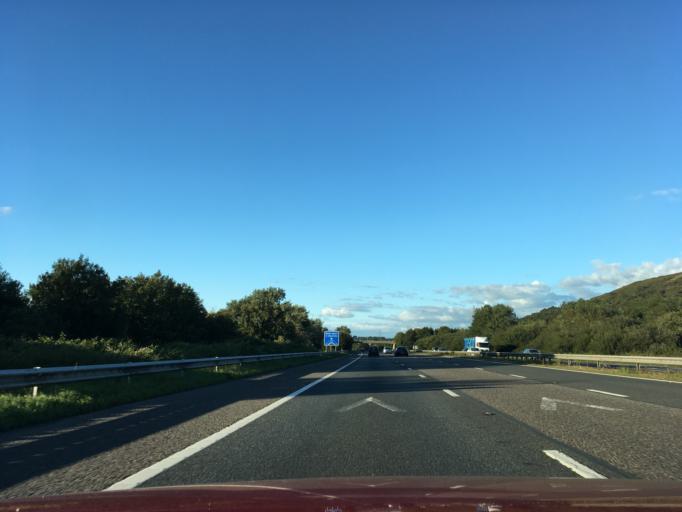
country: GB
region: England
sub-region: North Somerset
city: Banwell
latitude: 51.2919
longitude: -2.8966
